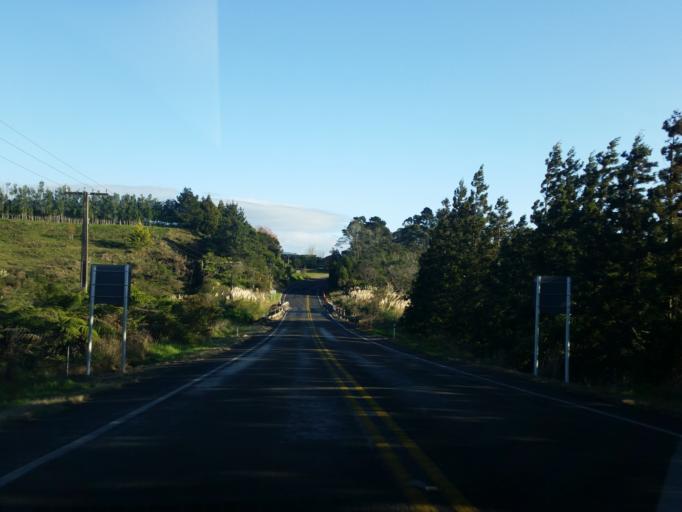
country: NZ
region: Bay of Plenty
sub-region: Western Bay of Plenty District
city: Katikati
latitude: -37.6348
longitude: 175.9608
